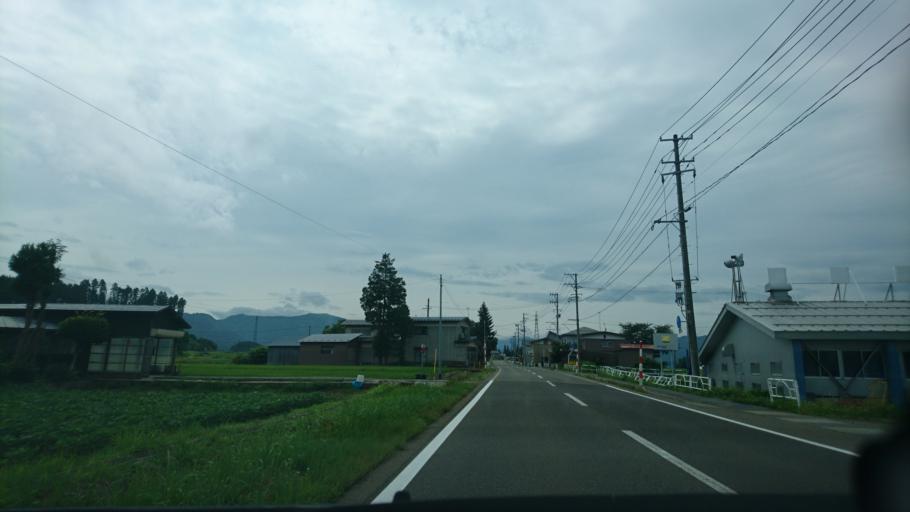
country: JP
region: Akita
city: Yuzawa
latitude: 39.1849
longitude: 140.5532
